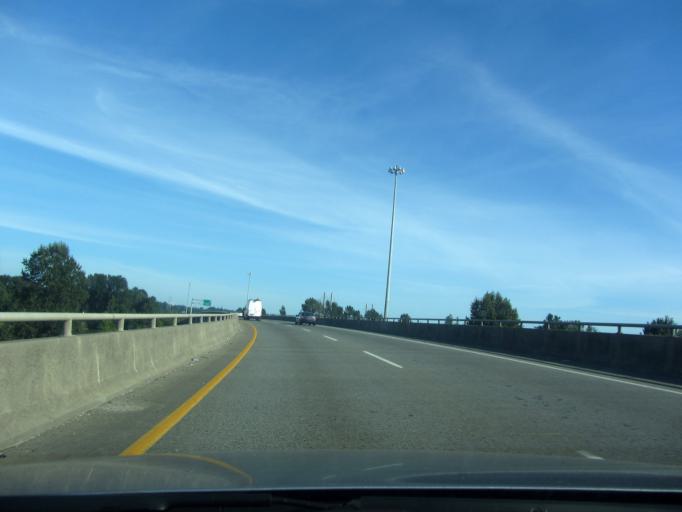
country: CA
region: British Columbia
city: New Westminster
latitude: 49.1759
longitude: -122.9604
